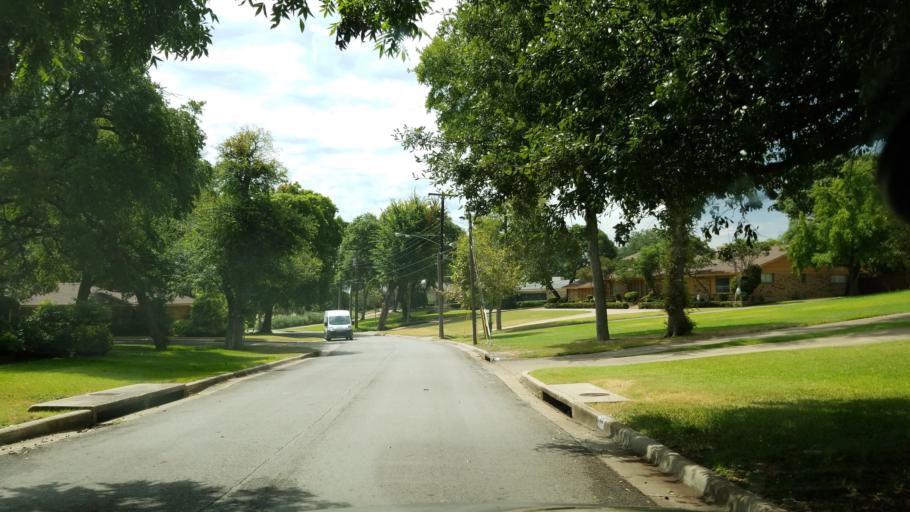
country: US
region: Texas
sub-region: Dallas County
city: Duncanville
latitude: 32.6710
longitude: -96.8493
